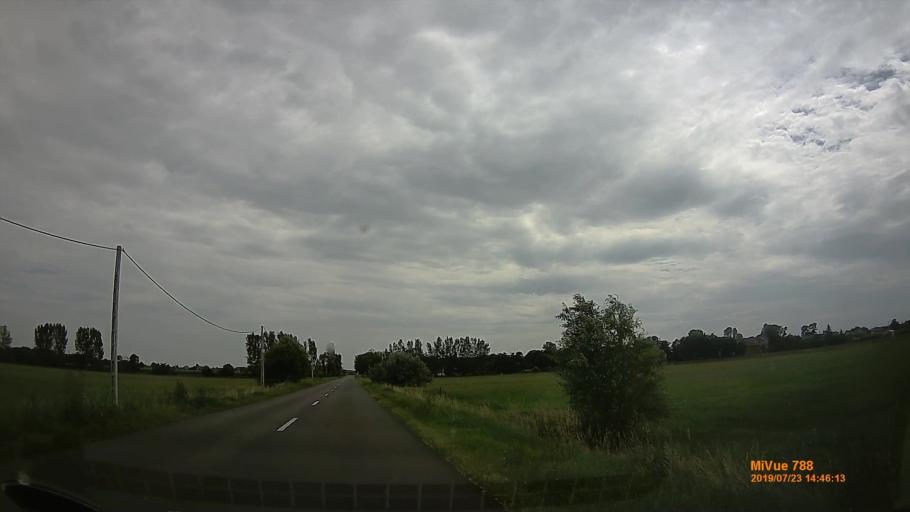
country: HU
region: Szabolcs-Szatmar-Bereg
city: Nyiregyhaza
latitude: 47.9211
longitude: 21.6768
